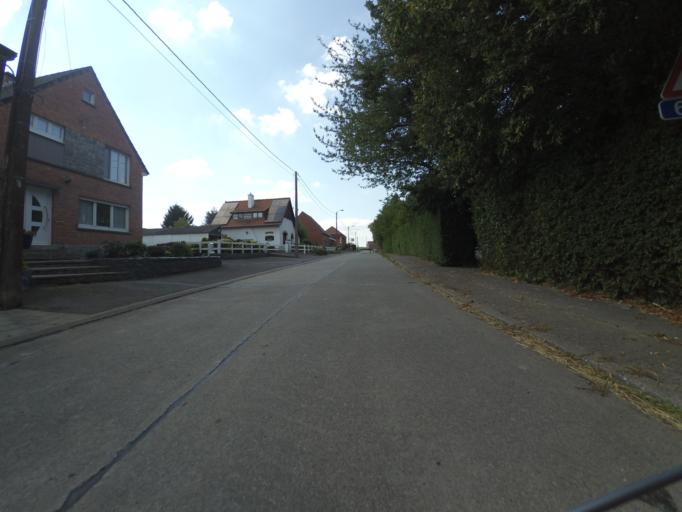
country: BE
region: Wallonia
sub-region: Province du Hainaut
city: Frasnes-lez-Buissenal
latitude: 50.6844
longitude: 3.5578
